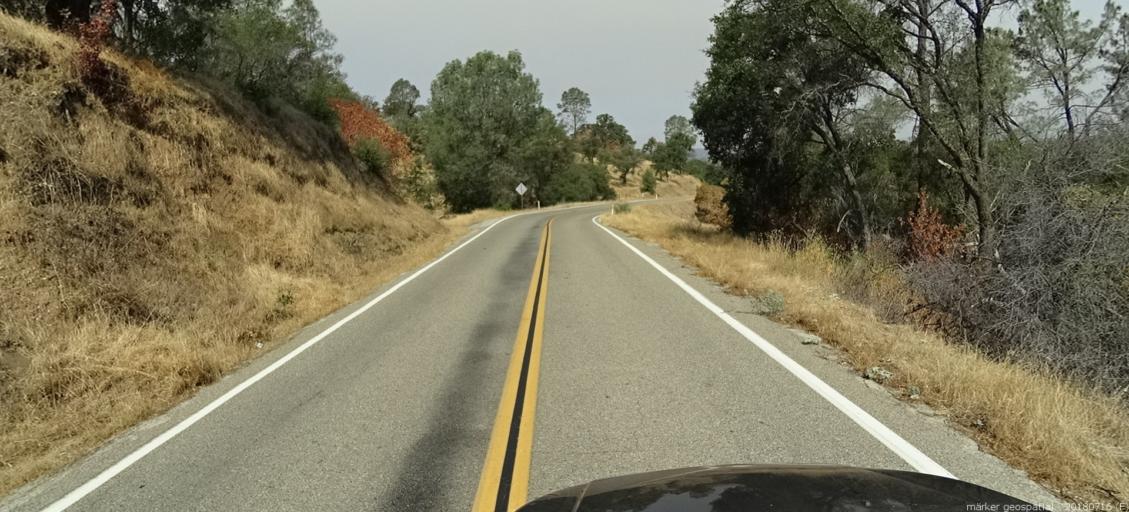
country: US
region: California
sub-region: Madera County
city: Yosemite Lakes
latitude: 37.2394
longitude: -119.8314
